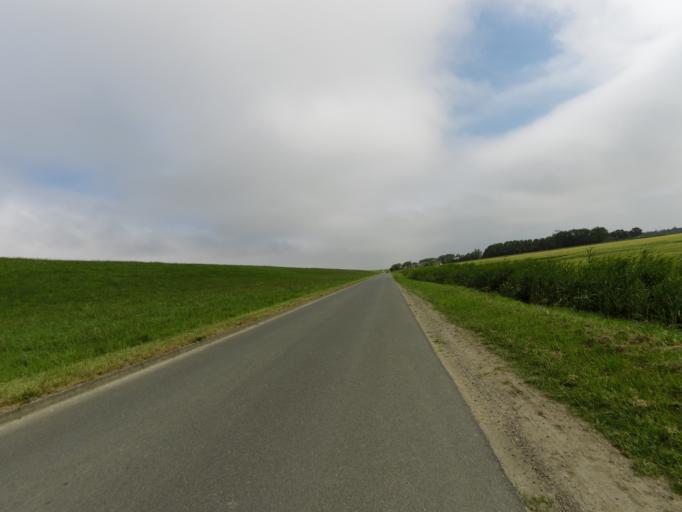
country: DE
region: Lower Saxony
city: Padingbuttel
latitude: 53.7492
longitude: 8.5296
